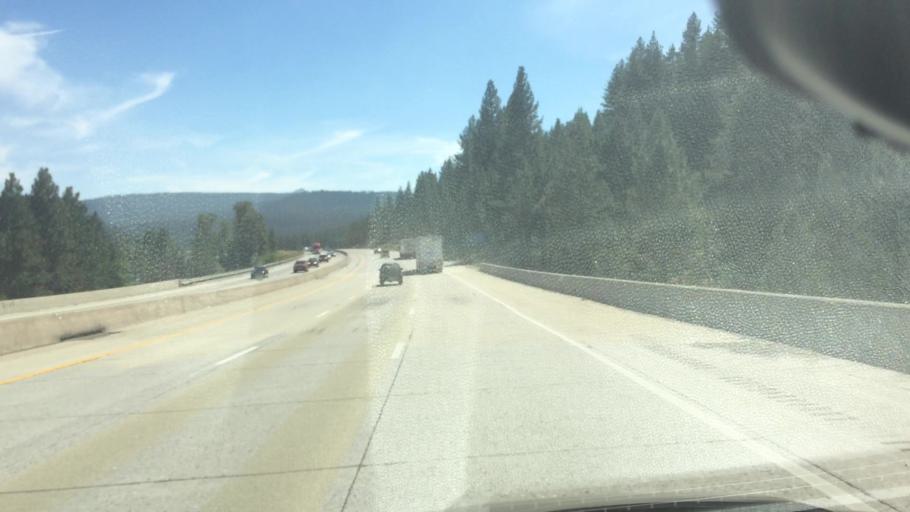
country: US
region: California
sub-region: Nevada County
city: Truckee
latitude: 39.3311
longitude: -120.1862
